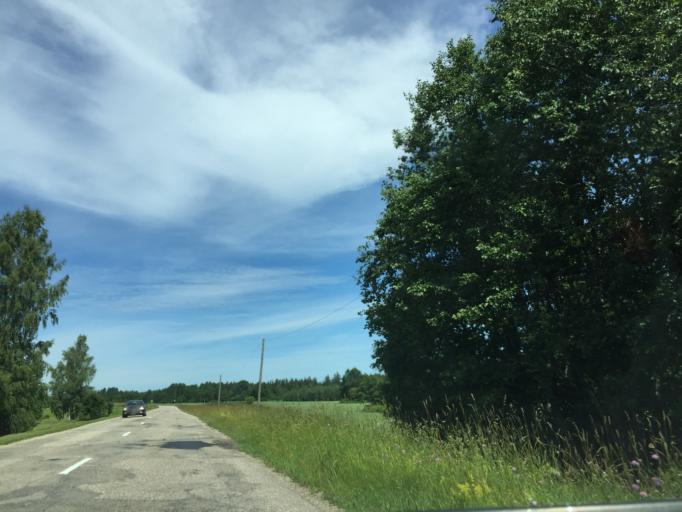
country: LV
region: Dundaga
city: Dundaga
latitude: 57.5386
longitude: 22.3293
